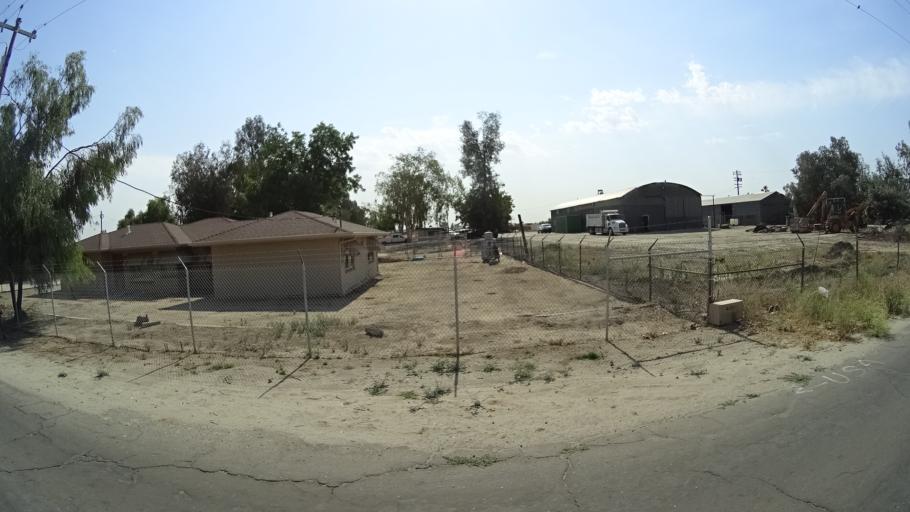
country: US
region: California
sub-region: Fresno County
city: West Park
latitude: 36.7424
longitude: -119.8533
